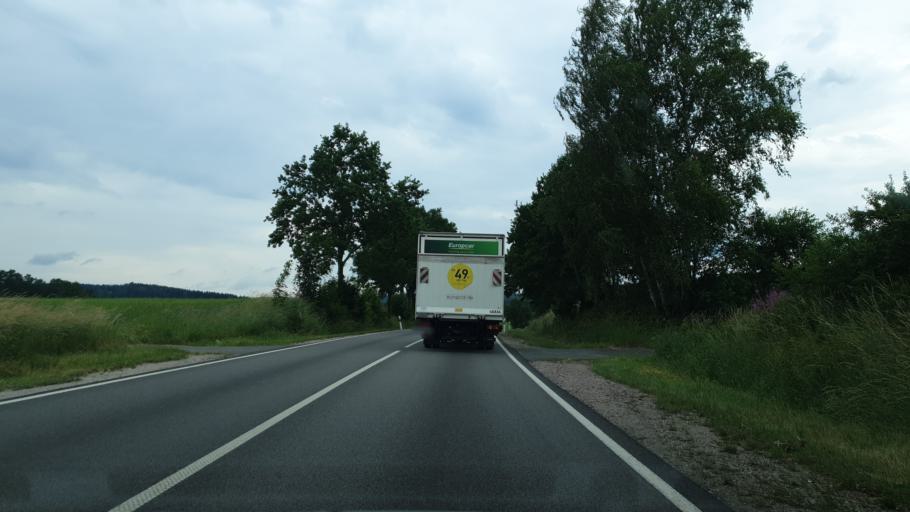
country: DE
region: Saxony
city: Waldkirchen
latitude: 50.5731
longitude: 12.3890
